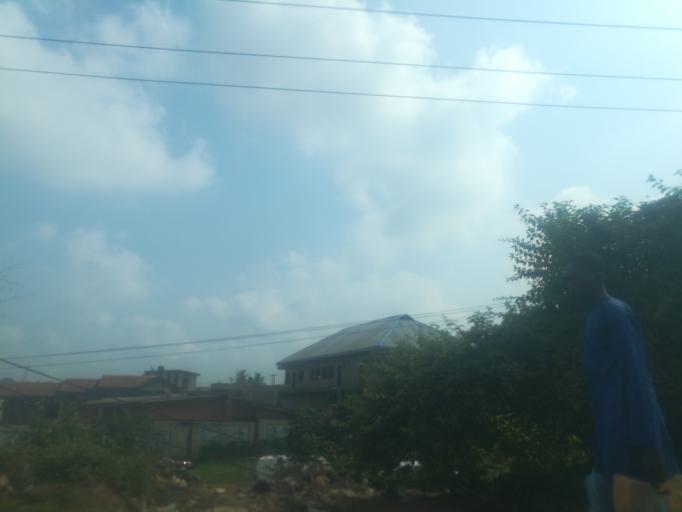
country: NG
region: Oyo
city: Ibadan
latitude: 7.4180
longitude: 3.9415
